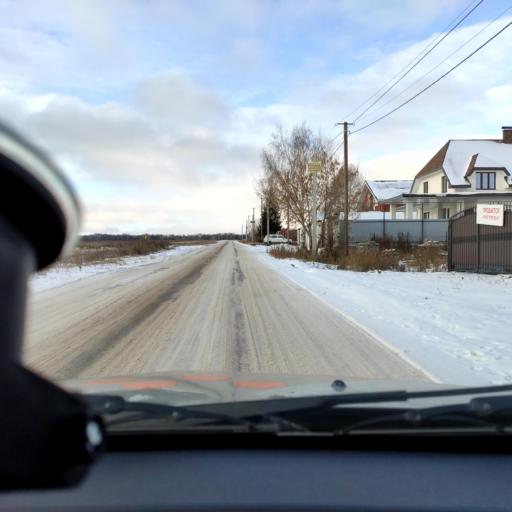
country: RU
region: Bashkortostan
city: Avdon
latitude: 54.7834
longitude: 55.7328
